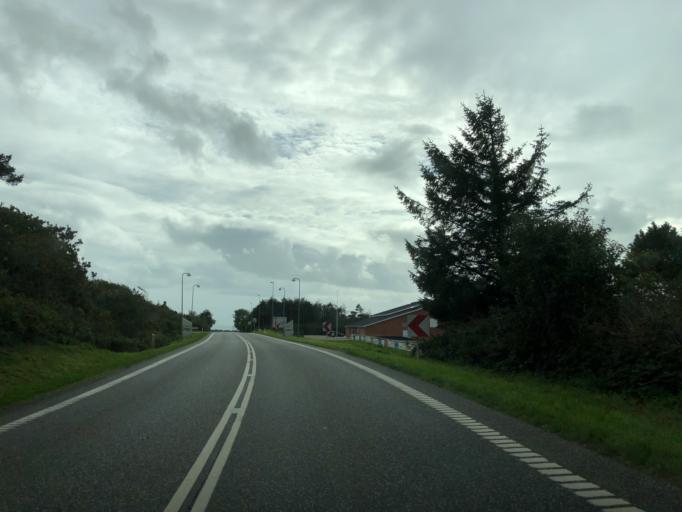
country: DK
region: North Denmark
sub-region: Thisted Kommune
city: Hurup
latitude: 56.7115
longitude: 8.4130
